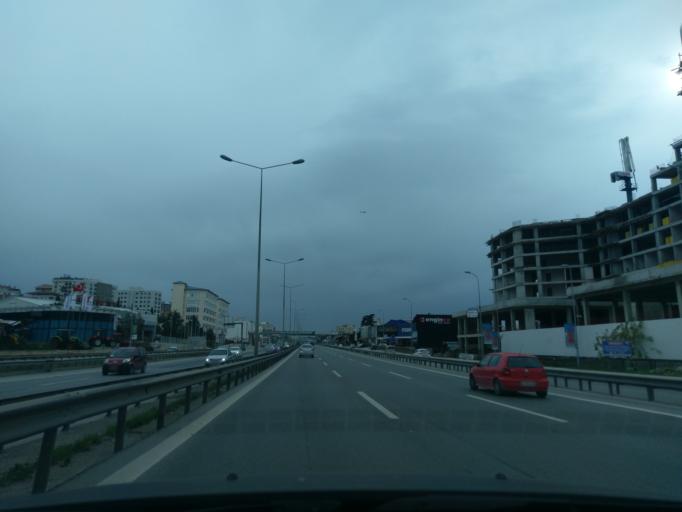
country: TR
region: Istanbul
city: Pendik
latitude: 40.8942
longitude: 29.2296
